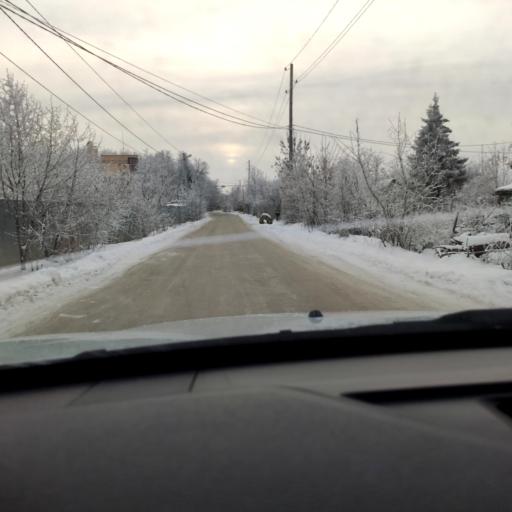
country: RU
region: Samara
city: Petra-Dubrava
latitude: 53.2999
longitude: 50.2509
